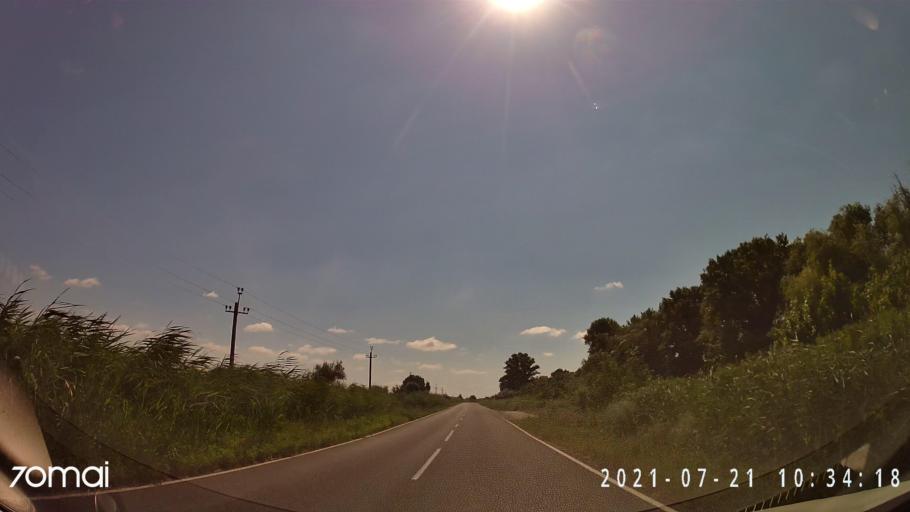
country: RO
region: Tulcea
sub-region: Oras Isaccea
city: Isaccea
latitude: 45.2959
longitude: 28.4442
